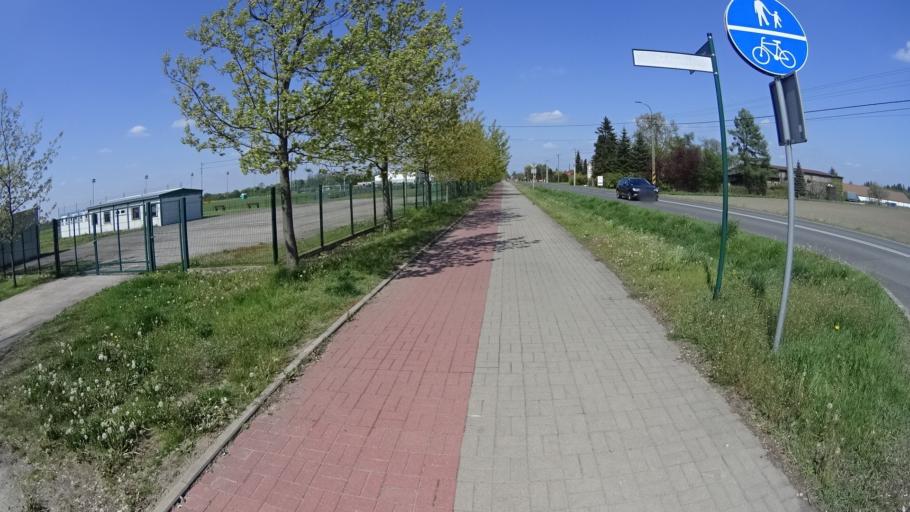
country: PL
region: Masovian Voivodeship
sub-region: Powiat warszawski zachodni
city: Stare Babice
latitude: 52.2434
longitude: 20.8187
